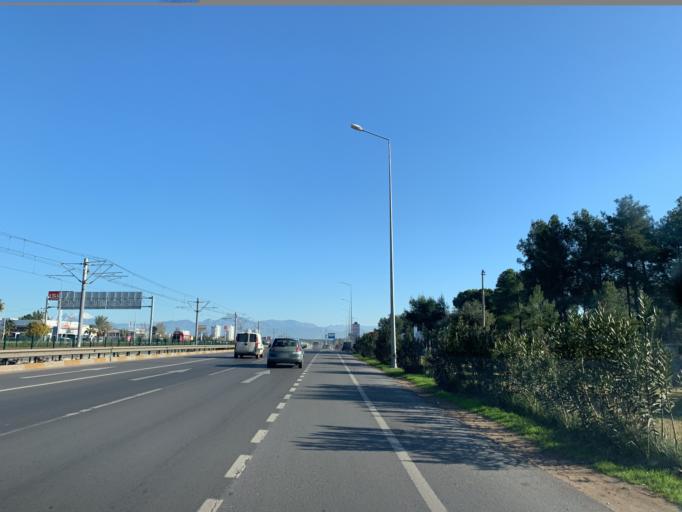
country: TR
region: Antalya
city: Aksu
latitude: 36.9327
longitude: 30.8095
